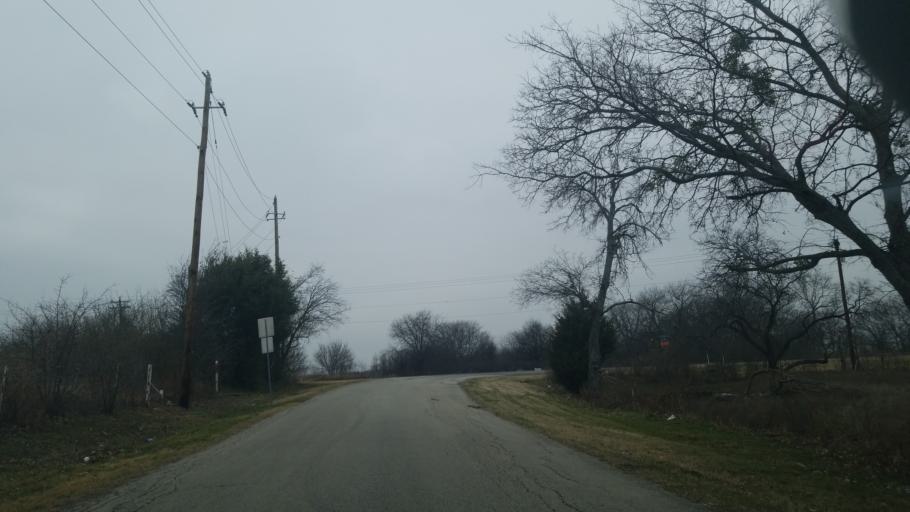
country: US
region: Texas
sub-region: Denton County
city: Argyle
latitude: 33.1473
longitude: -97.1683
